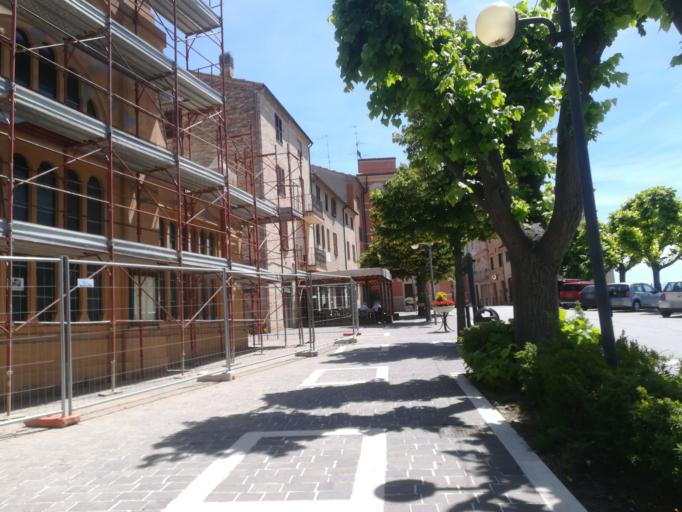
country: IT
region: The Marches
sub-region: Provincia di Macerata
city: Mogliano
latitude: 43.1854
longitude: 13.4782
